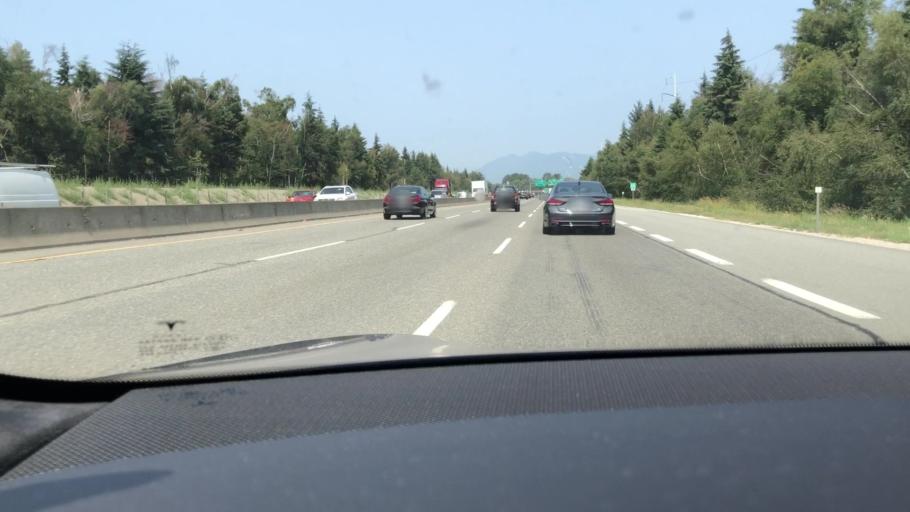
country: CA
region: British Columbia
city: Richmond
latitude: 49.1598
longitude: -123.0865
